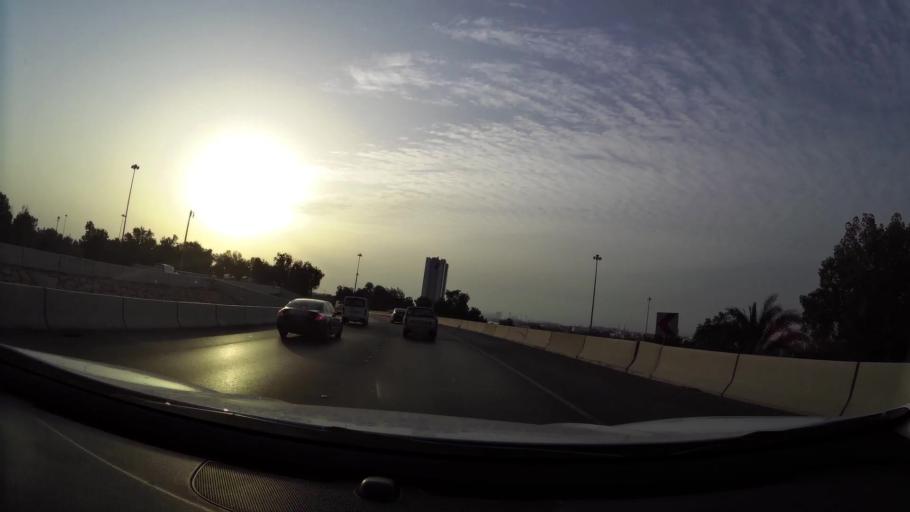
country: AE
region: Abu Dhabi
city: Abu Dhabi
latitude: 24.3948
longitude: 54.5245
